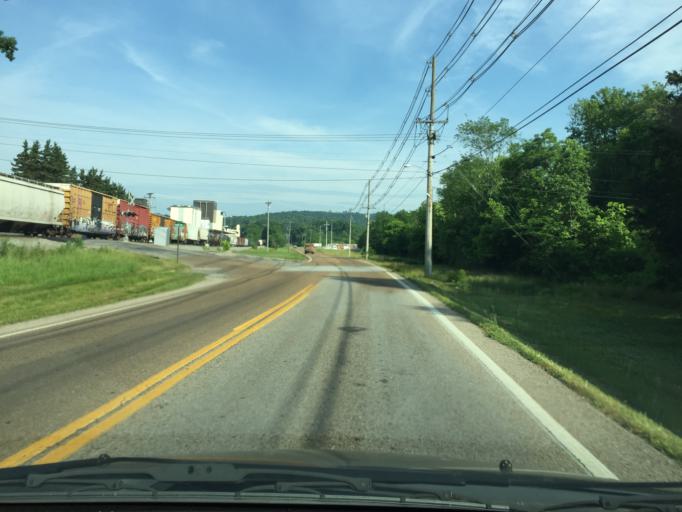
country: US
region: Tennessee
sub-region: Hamilton County
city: Collegedale
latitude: 35.0480
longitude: -85.0374
